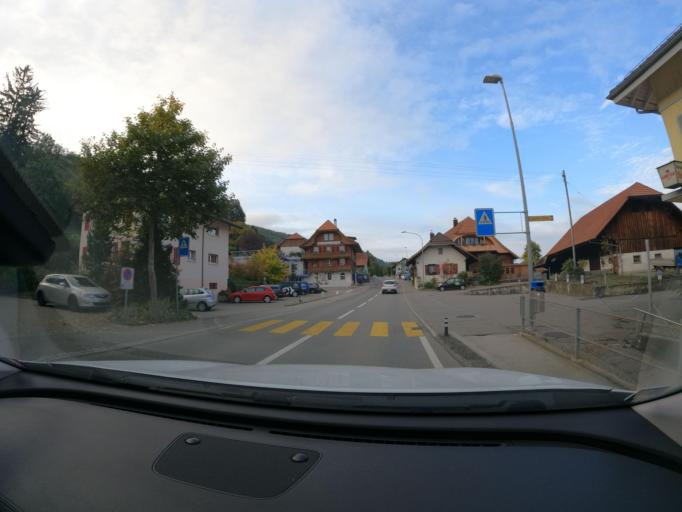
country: CH
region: Bern
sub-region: Bern-Mittelland District
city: Toffen
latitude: 46.8610
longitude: 7.4905
